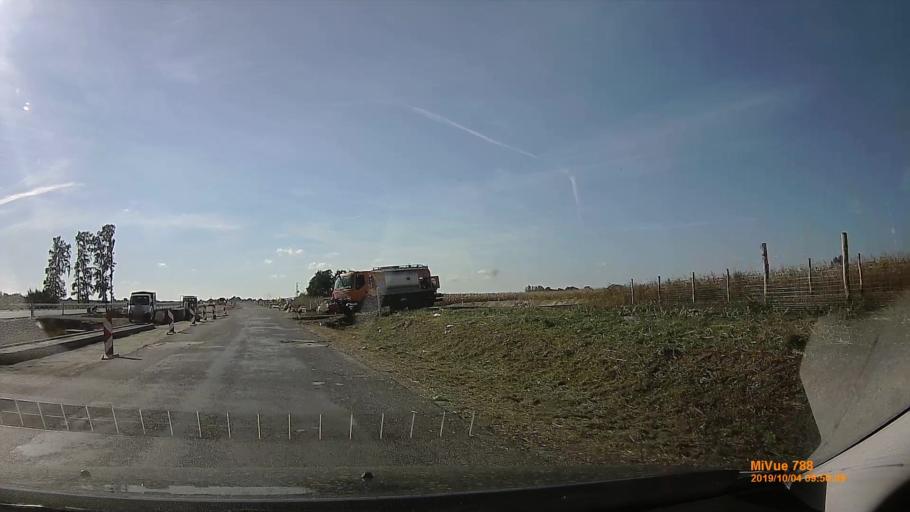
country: HU
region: Somogy
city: Kaposvar
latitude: 46.4384
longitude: 17.7705
